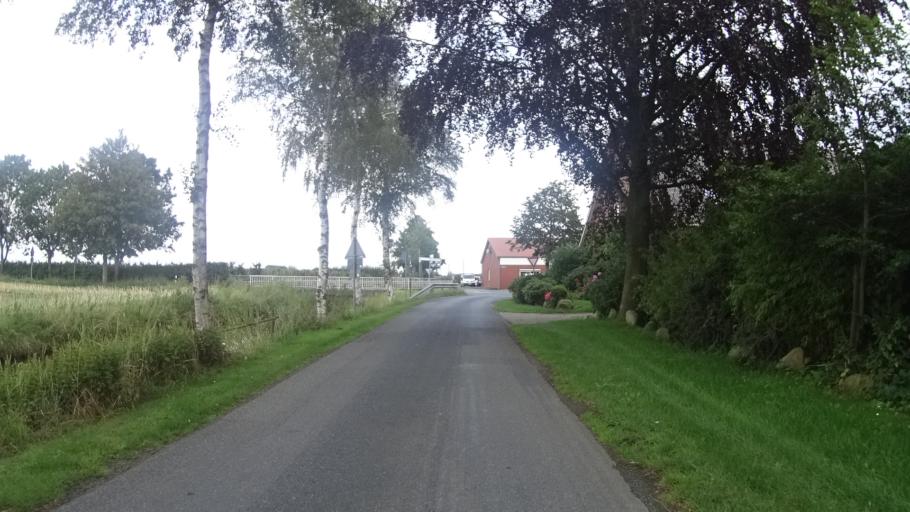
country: DE
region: Lower Saxony
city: Grossenworden
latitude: 53.7020
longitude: 9.2539
